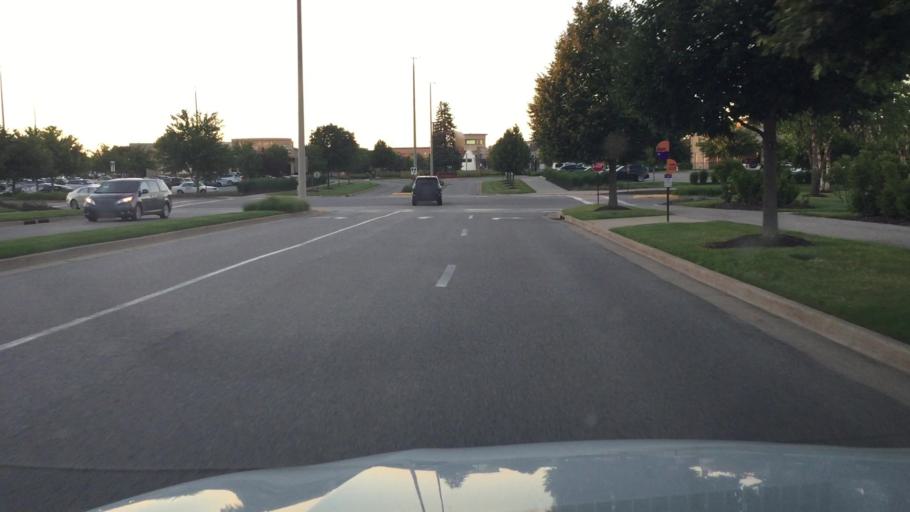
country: US
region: Iowa
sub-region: Polk County
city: Clive
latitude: 41.5648
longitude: -93.8039
